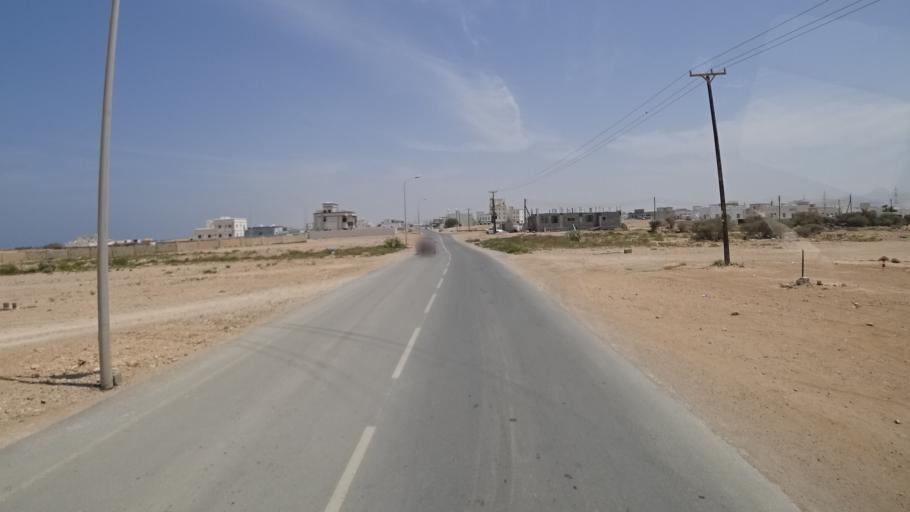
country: OM
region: Ash Sharqiyah
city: Sur
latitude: 22.6178
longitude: 59.4595
